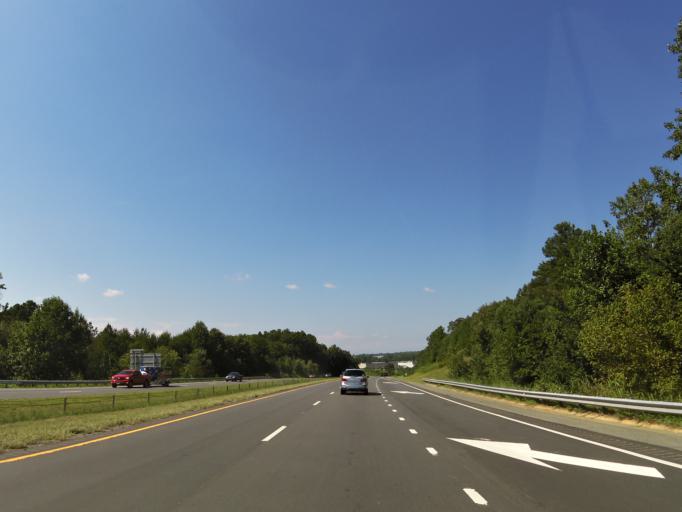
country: US
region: North Carolina
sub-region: Catawba County
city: Maiden
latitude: 35.5320
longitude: -81.2248
